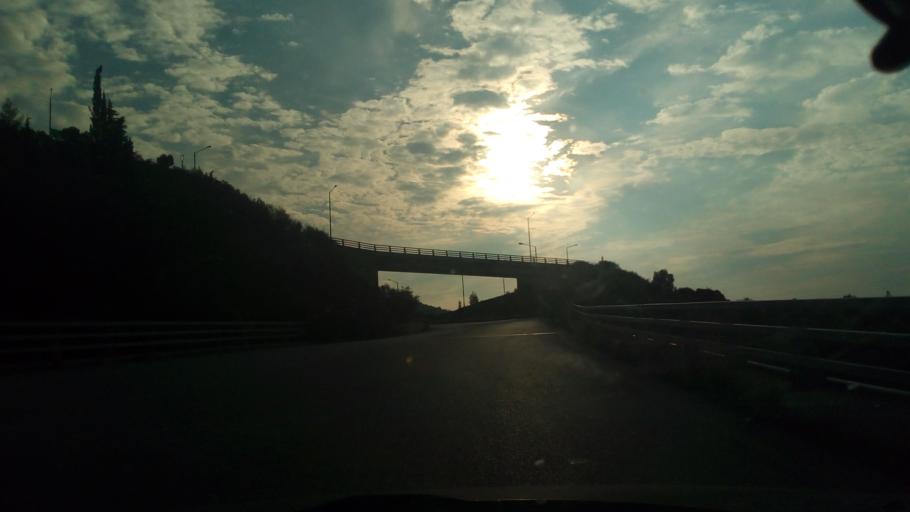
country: GR
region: West Greece
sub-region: Nomos Aitolias kai Akarnanias
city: Nafpaktos
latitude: 38.4000
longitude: 21.7999
